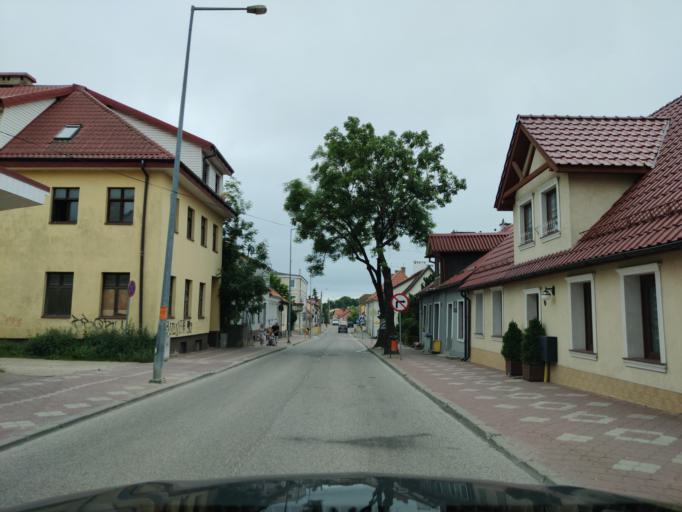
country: PL
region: Warmian-Masurian Voivodeship
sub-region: Powiat gizycki
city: Ryn
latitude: 53.9375
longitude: 21.5466
